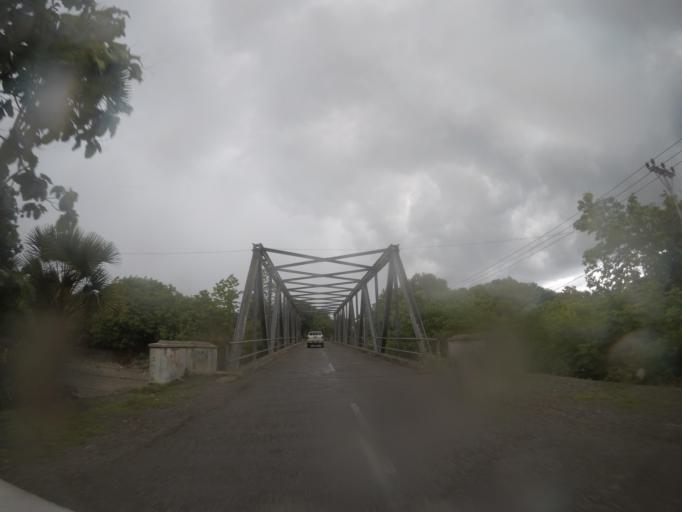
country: ID
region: East Nusa Tenggara
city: Atambua
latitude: -8.9650
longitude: 124.9976
